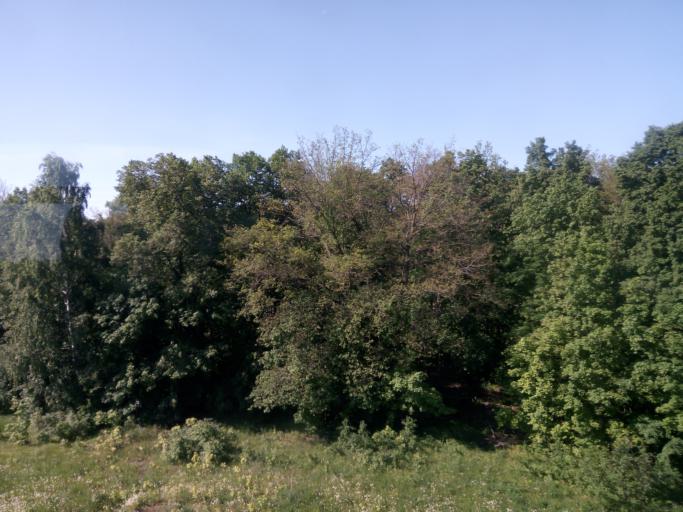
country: RU
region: Tatarstan
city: Stolbishchi
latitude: 55.6126
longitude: 49.2910
